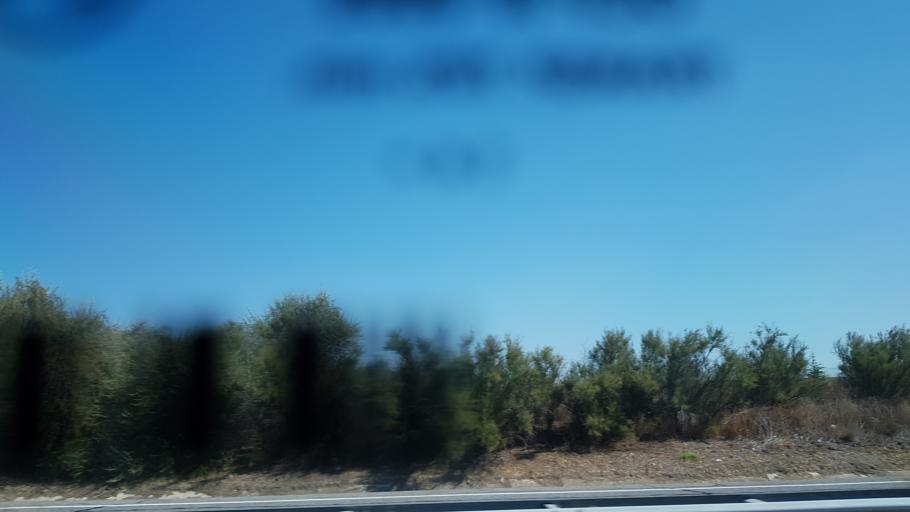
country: TR
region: Kirklareli
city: Luleburgaz
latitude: 41.4097
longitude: 27.3867
